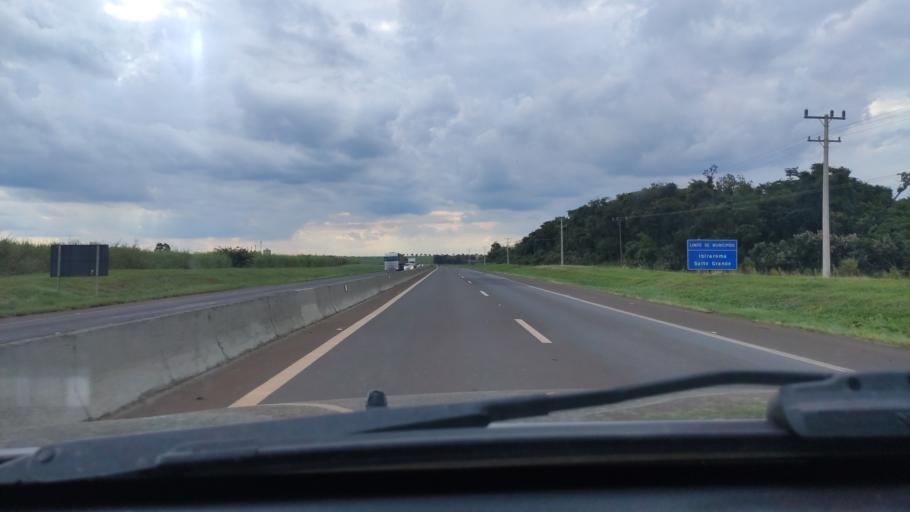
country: BR
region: Sao Paulo
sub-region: Palmital
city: Palmital
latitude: -22.8330
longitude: -50.0247
